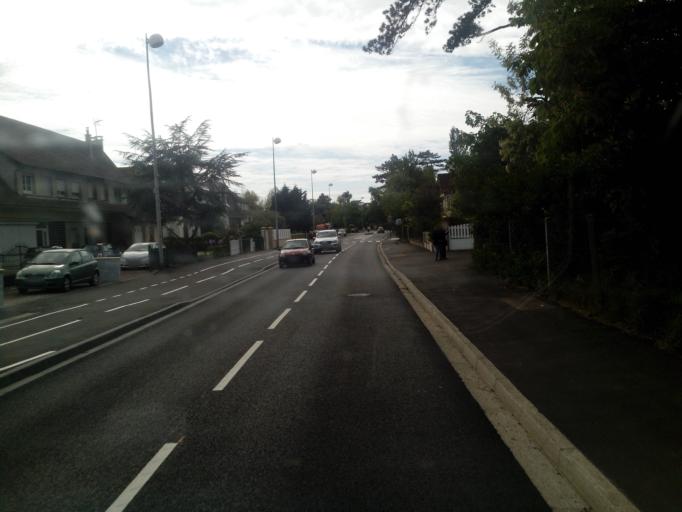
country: FR
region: Lower Normandy
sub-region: Departement du Calvados
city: Merville-Franceville-Plage
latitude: 49.2846
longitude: -0.1587
